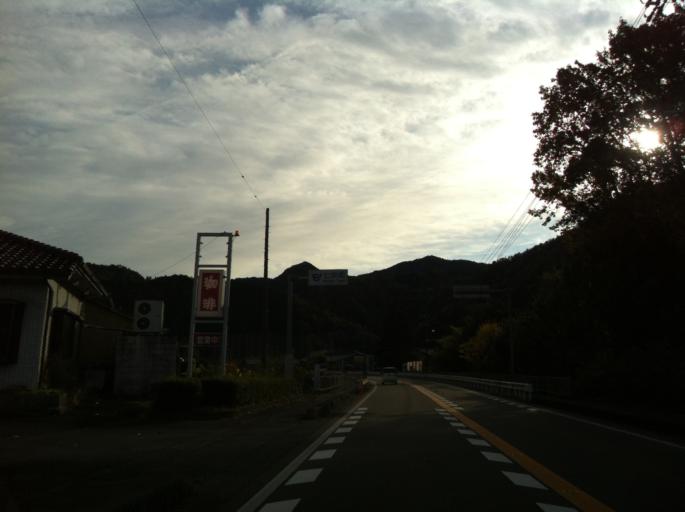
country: JP
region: Gifu
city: Minokamo
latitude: 35.5207
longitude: 137.1062
